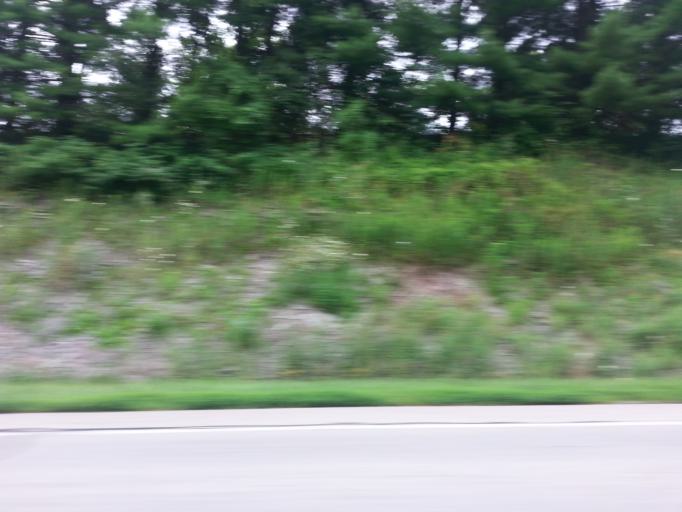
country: US
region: Ohio
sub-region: Brown County
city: Georgetown
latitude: 38.8327
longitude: -83.8363
